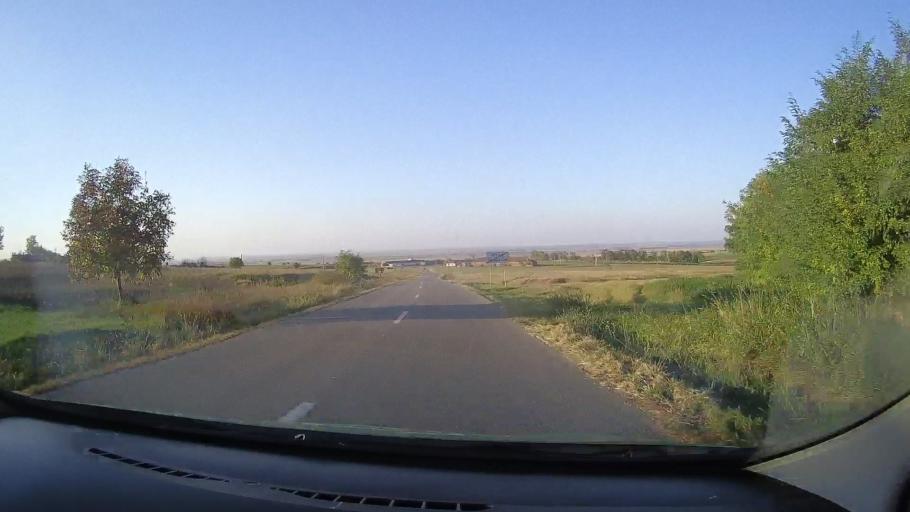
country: RO
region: Bihor
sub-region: Comuna Cetariu
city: Cetariu
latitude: 47.1499
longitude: 21.9942
